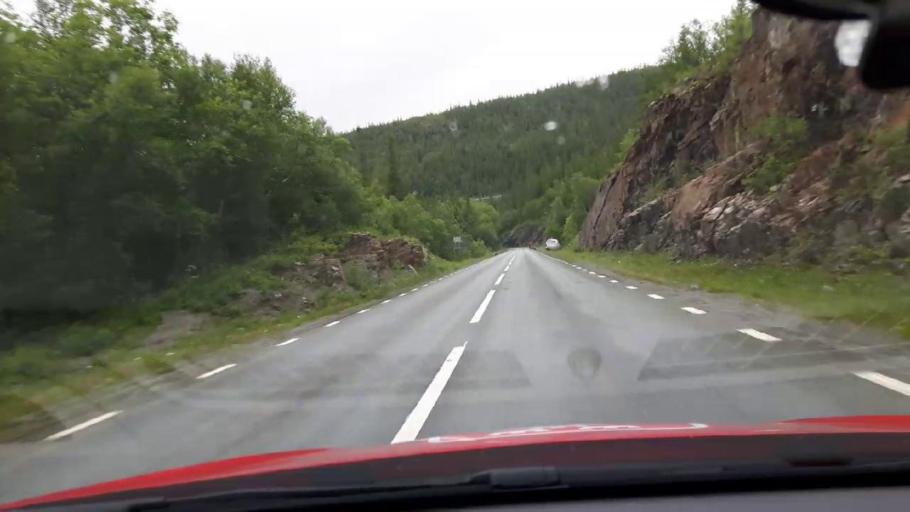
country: NO
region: Nord-Trondelag
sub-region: Meraker
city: Meraker
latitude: 63.3311
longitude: 12.0591
